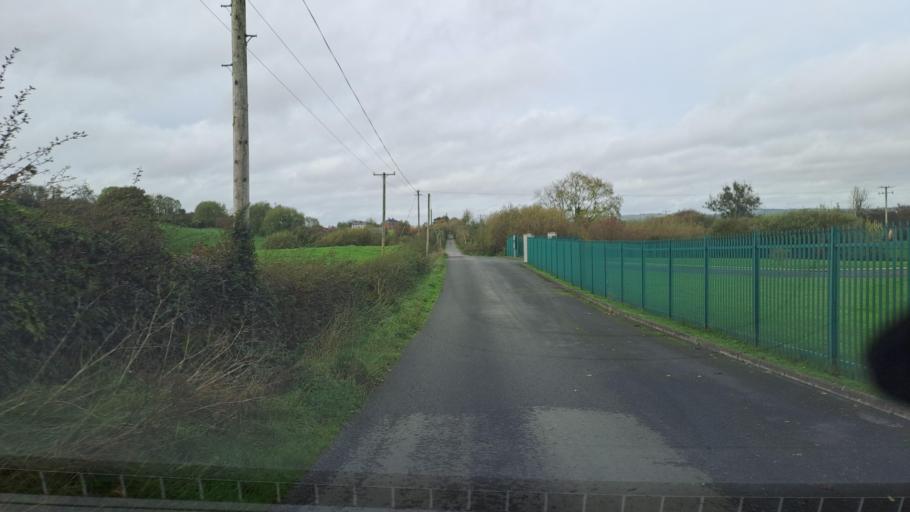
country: IE
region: Ulster
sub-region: An Cabhan
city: Kingscourt
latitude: 54.0219
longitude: -6.8249
